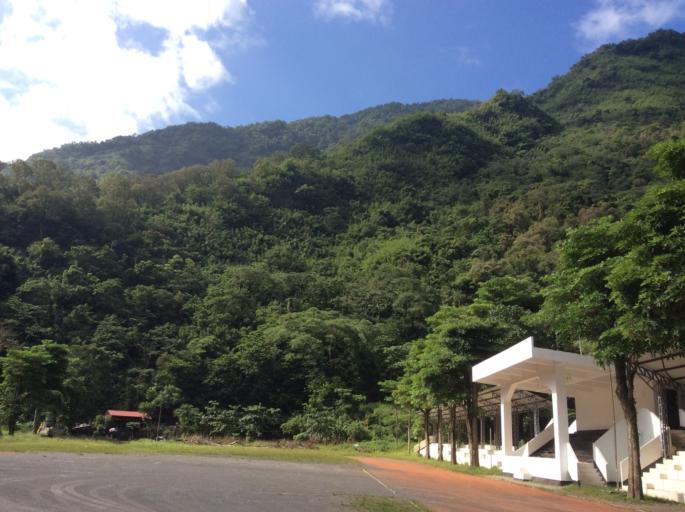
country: TW
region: Taiwan
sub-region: Pingtung
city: Pingtung
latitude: 22.9092
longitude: 120.7143
